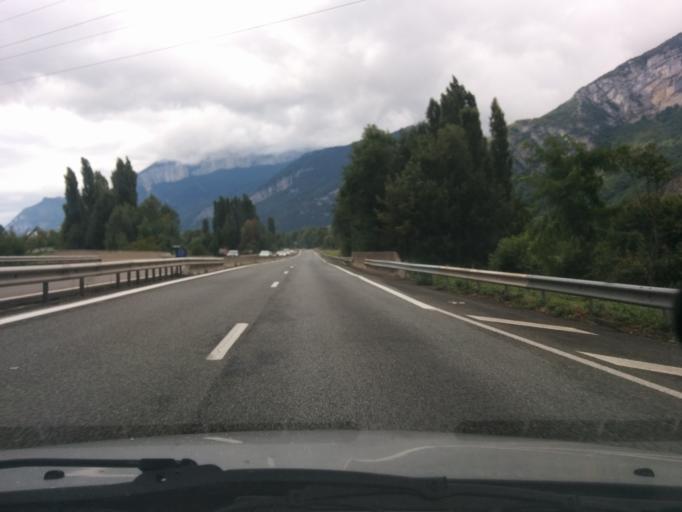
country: FR
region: Rhone-Alpes
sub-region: Departement de l'Isere
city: Voreppe
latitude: 45.2981
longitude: 5.6213
